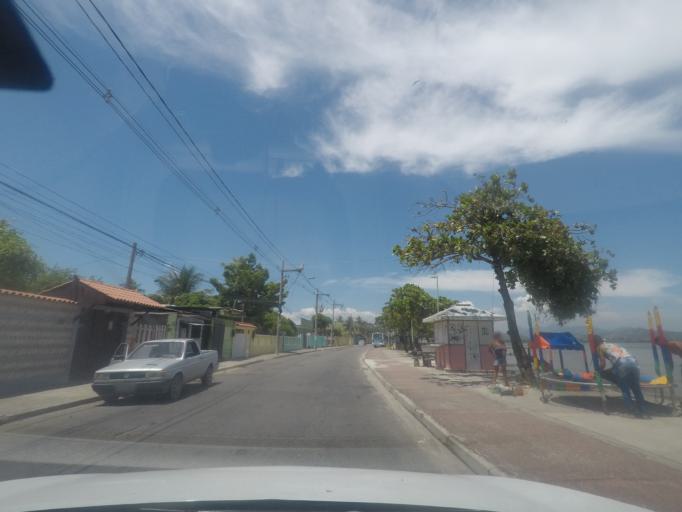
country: BR
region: Rio de Janeiro
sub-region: Itaguai
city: Itaguai
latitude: -22.9861
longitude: -43.6877
